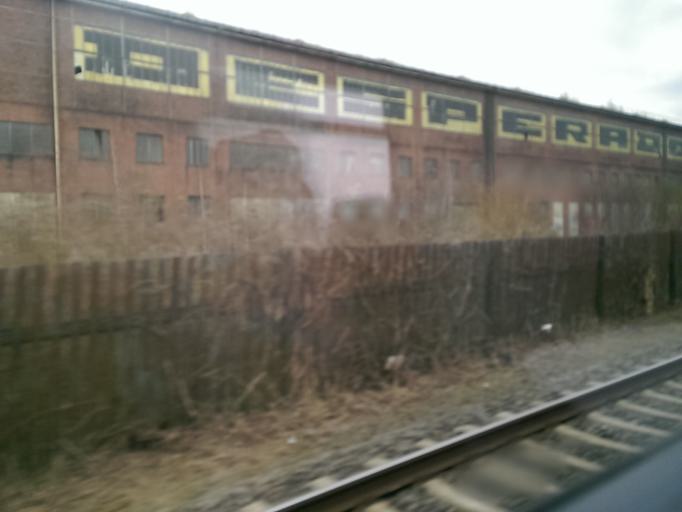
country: DE
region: North Rhine-Westphalia
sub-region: Regierungsbezirk Arnsberg
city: Dortmund
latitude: 51.5318
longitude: 7.4787
